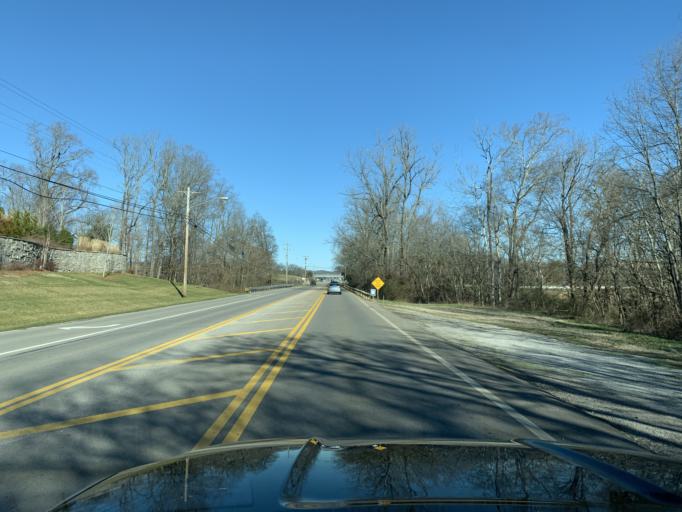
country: US
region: Tennessee
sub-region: Maury County
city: Spring Hill
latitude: 35.7255
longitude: -86.9244
